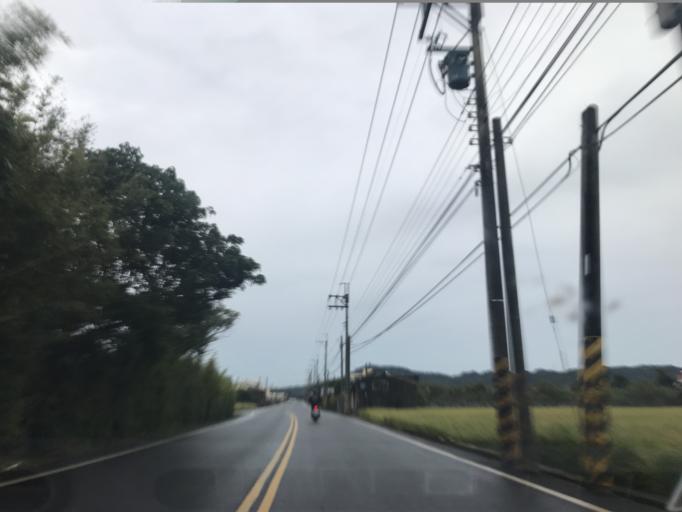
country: TW
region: Taiwan
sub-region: Hsinchu
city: Zhubei
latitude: 24.8407
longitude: 121.1185
